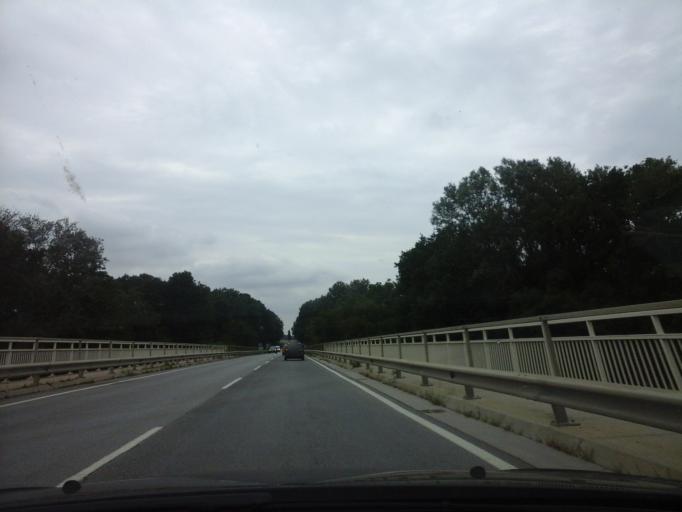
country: AT
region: Lower Austria
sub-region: Politischer Bezirk Ganserndorf
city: Engelhartstetten
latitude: 48.1561
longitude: 16.9014
